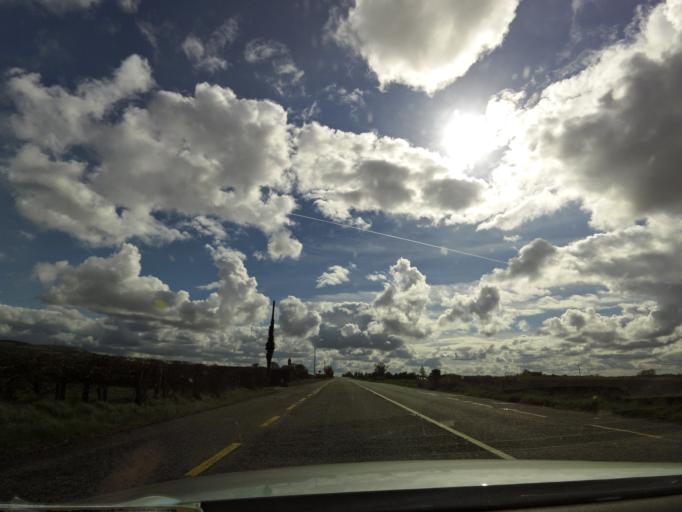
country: IE
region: Leinster
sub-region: Laois
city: Rathdowney
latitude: 52.7949
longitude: -7.5122
